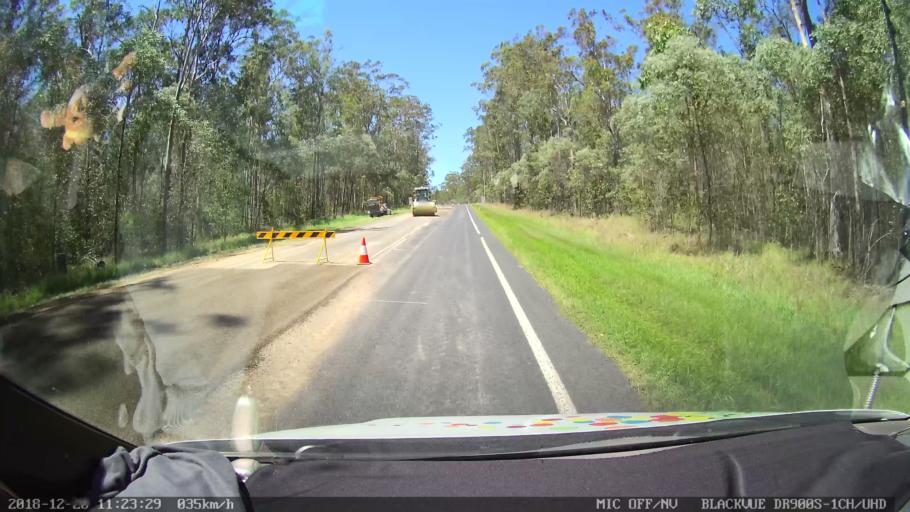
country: AU
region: New South Wales
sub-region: Richmond Valley
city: Casino
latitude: -29.0659
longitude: 153.0042
